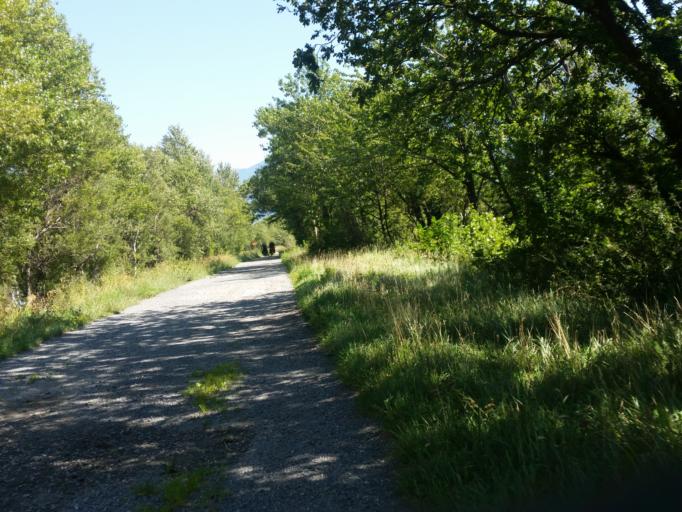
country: CH
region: Valais
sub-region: Martigny District
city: Martigny-Ville
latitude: 46.1202
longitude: 7.0716
